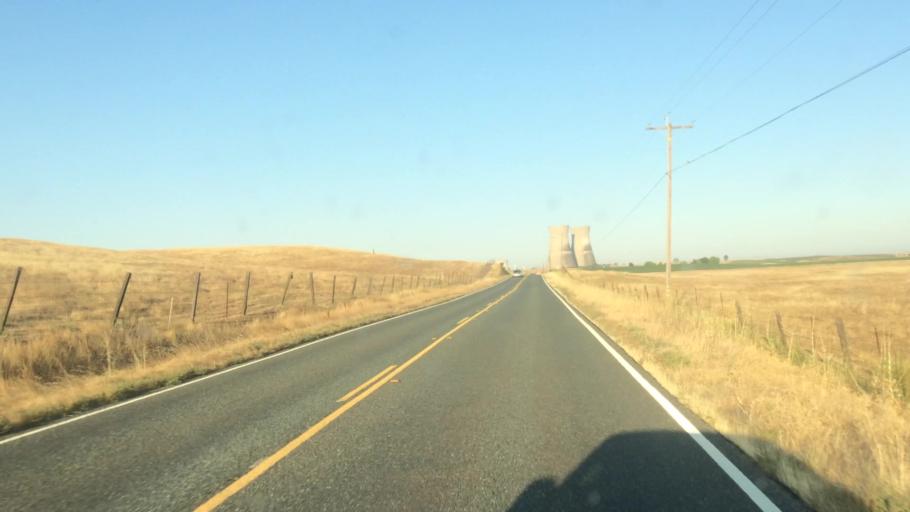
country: US
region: California
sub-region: Sacramento County
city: Clay
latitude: 38.3493
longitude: -121.0969
